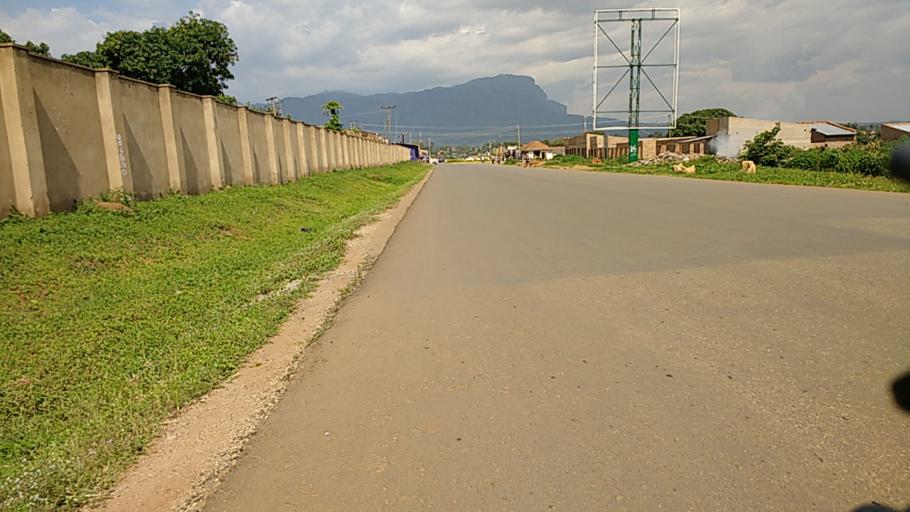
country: UG
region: Eastern Region
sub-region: Mbale District
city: Mbale
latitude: 1.0775
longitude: 34.1587
